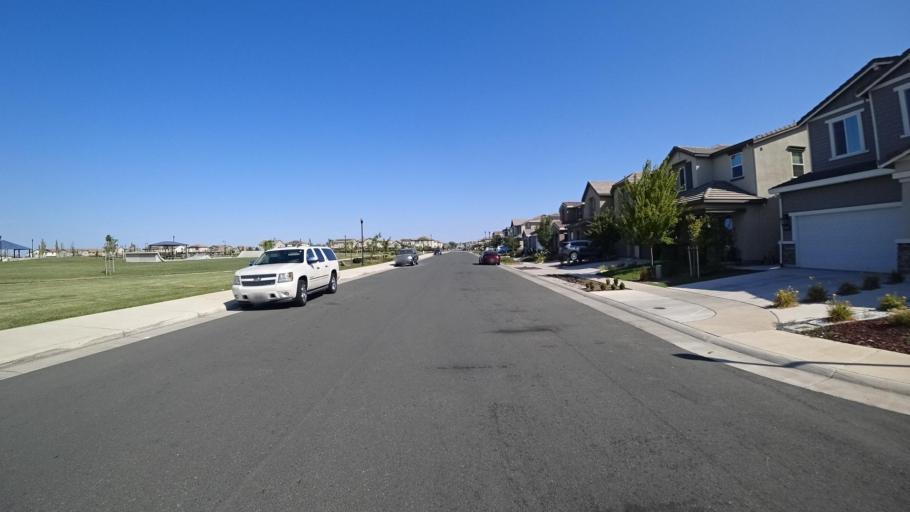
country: US
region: California
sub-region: Sacramento County
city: Elk Grove
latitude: 38.3824
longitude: -121.3763
